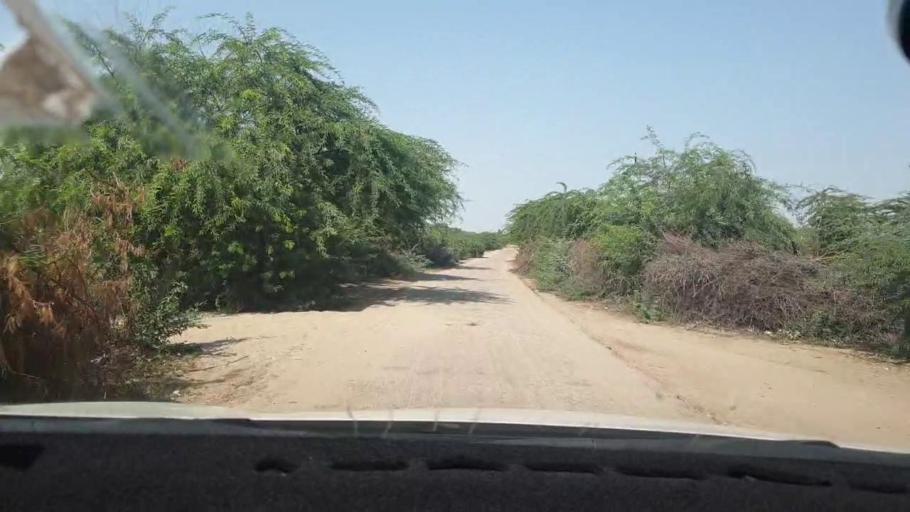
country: PK
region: Sindh
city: Tando Mittha Khan
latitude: 25.8775
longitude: 69.3870
